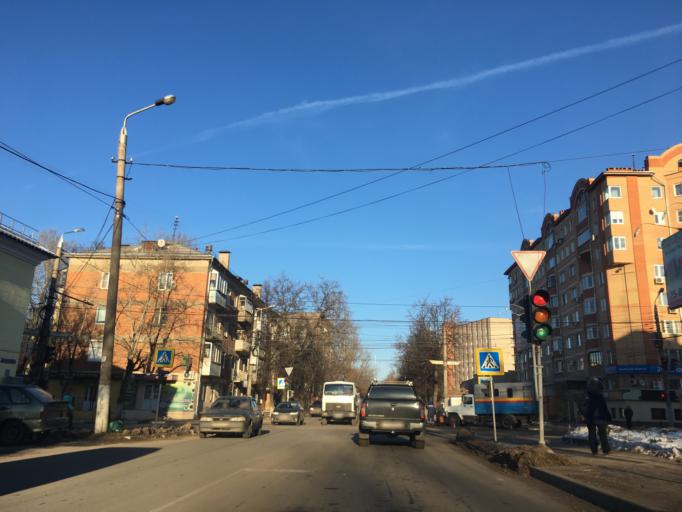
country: RU
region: Tula
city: Mendeleyevskiy
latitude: 54.1662
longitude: 37.5796
